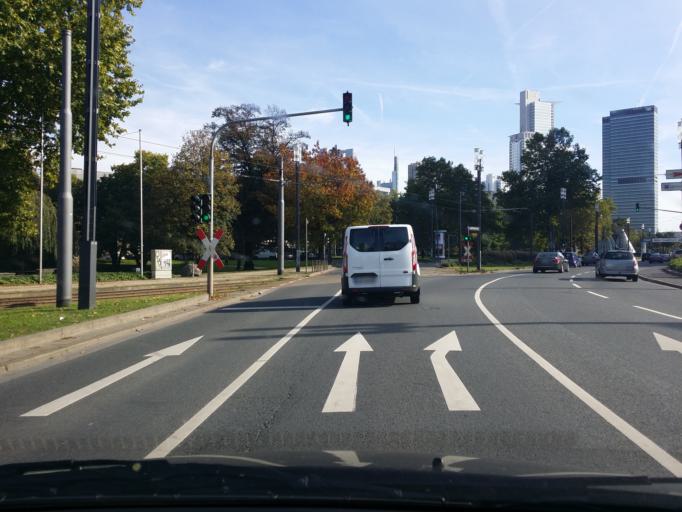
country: DE
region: Hesse
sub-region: Regierungsbezirk Darmstadt
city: Frankfurt am Main
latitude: 50.1133
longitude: 8.6515
